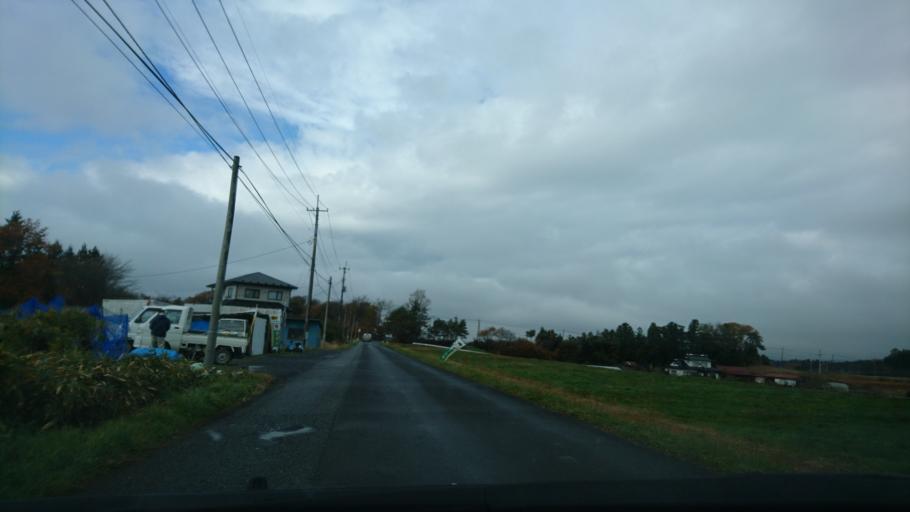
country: JP
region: Iwate
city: Ichinoseki
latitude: 38.8918
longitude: 141.1920
